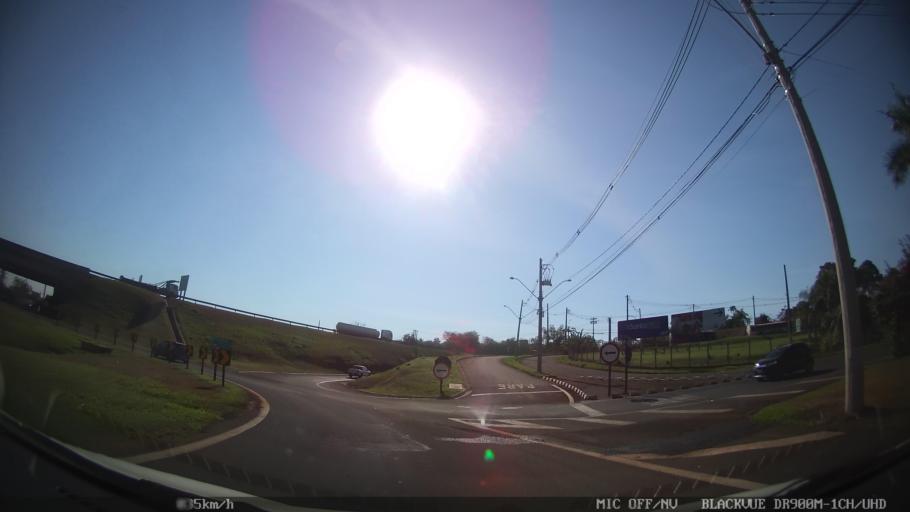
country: BR
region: Sao Paulo
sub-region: Ribeirao Preto
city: Ribeirao Preto
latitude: -21.2220
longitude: -47.7886
